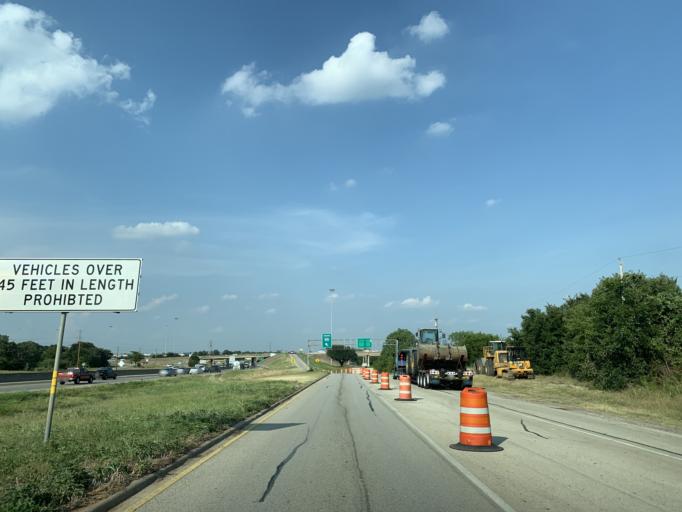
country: US
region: Texas
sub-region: Tarrant County
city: Richland Hills
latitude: 32.8032
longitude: -97.2157
